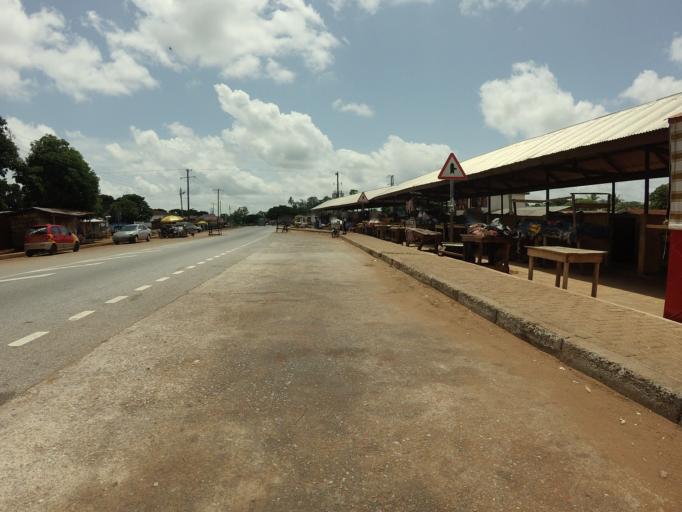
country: GH
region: Brong-Ahafo
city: Techiman
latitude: 7.7006
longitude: -1.8457
